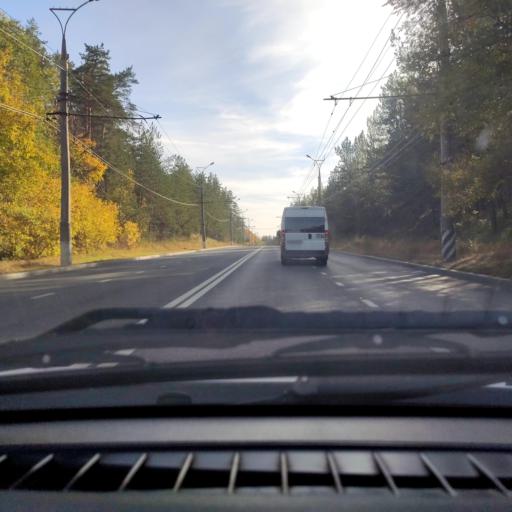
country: RU
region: Samara
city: Zhigulevsk
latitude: 53.4951
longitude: 49.4630
